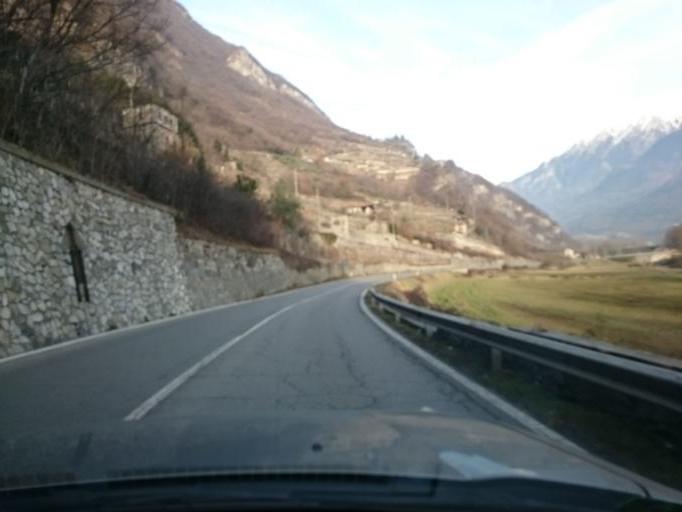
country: IT
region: Lombardy
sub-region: Provincia di Brescia
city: Malegno
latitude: 45.9566
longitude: 10.2837
